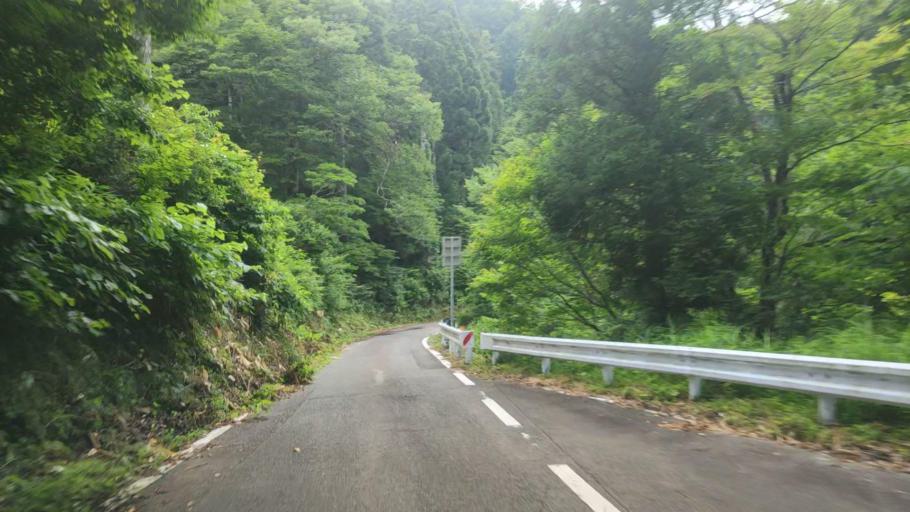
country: JP
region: Fukui
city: Katsuyama
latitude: 36.1973
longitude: 136.5248
